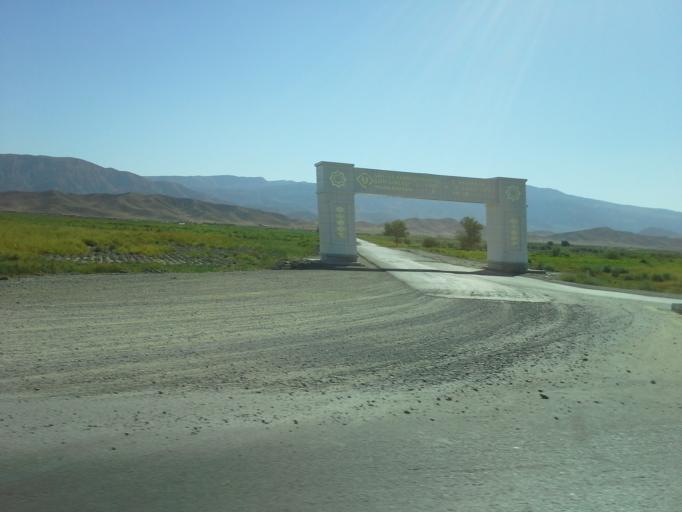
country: TM
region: Ahal
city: Baharly
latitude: 38.3493
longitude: 57.5504
